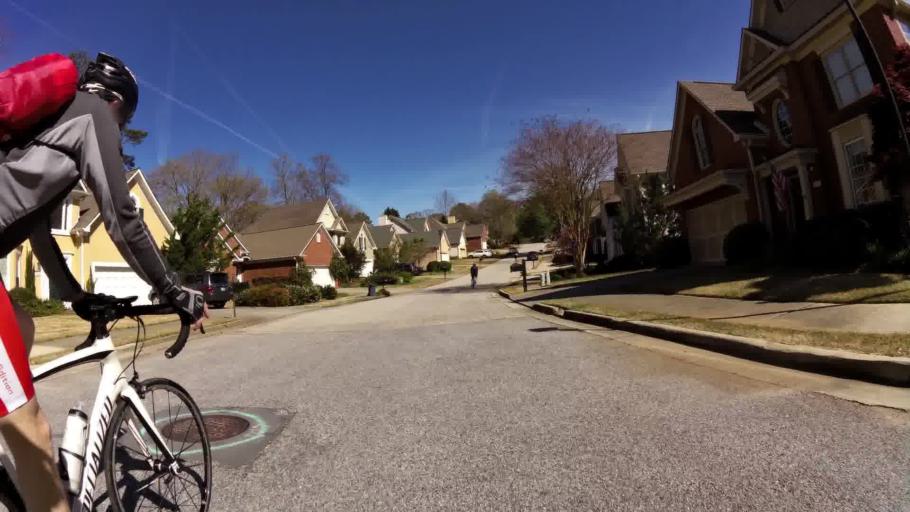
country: US
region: Georgia
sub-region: DeKalb County
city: Clarkston
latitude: 33.8229
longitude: -84.2666
